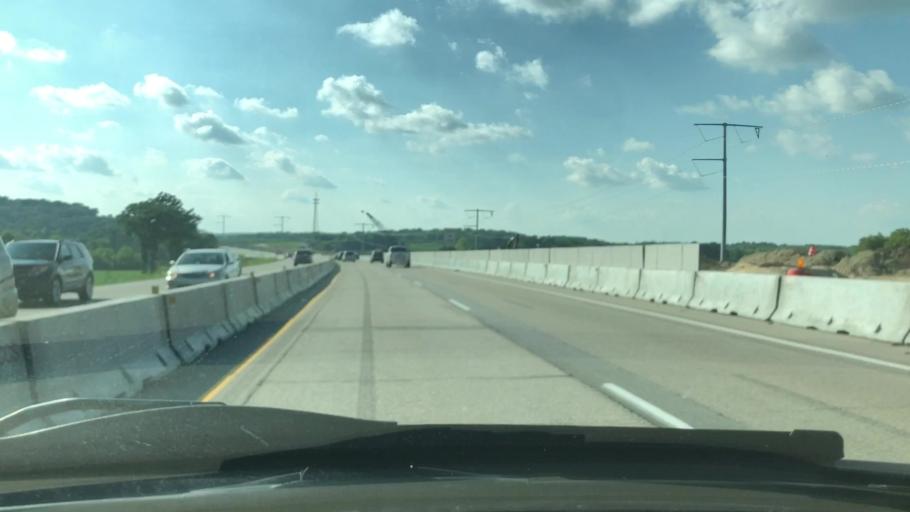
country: US
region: Wisconsin
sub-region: Dane County
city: Deerfield
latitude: 42.9900
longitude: -89.1368
